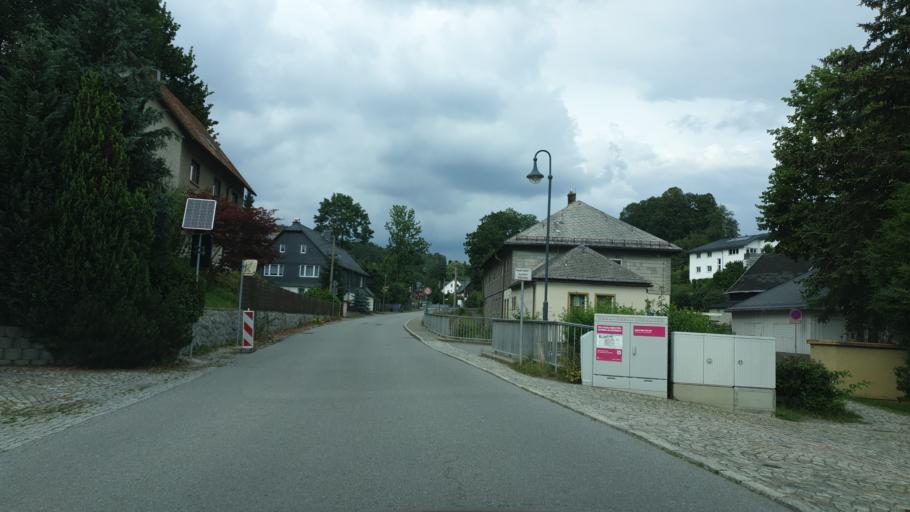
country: DE
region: Saxony
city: Lossnitz
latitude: 50.6428
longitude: 12.7556
